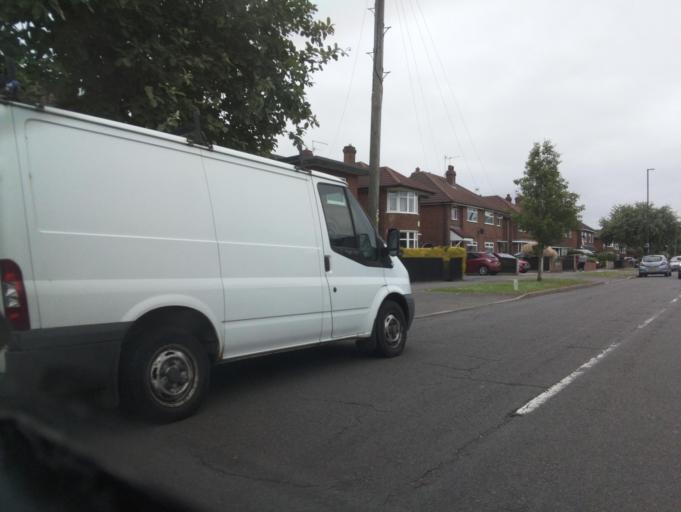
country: GB
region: England
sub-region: Derby
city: Derby
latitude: 52.9245
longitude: -1.5165
